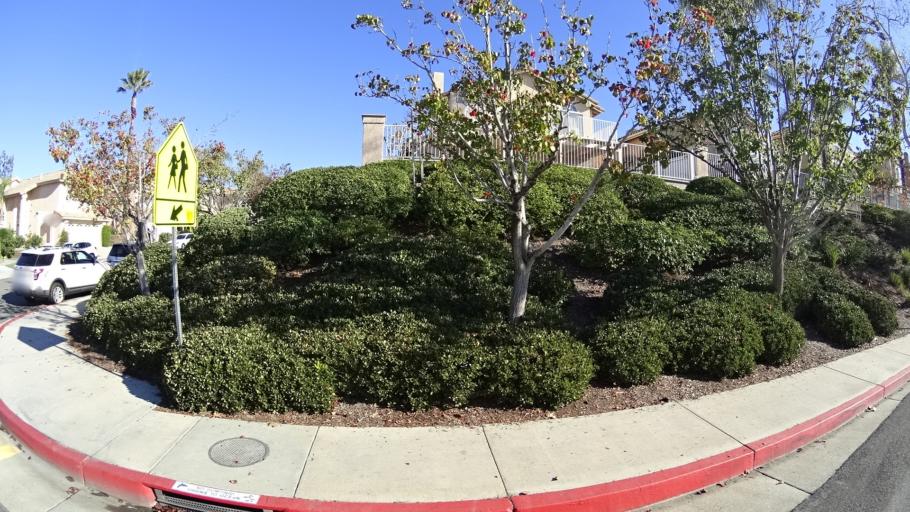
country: US
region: California
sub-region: Orange County
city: Foothill Ranch
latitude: 33.6825
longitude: -117.6605
